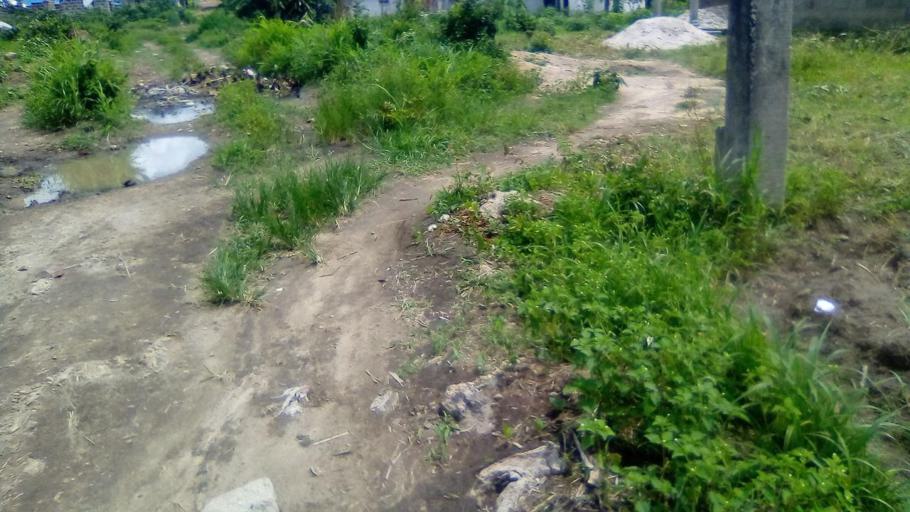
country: SL
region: Southern Province
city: Bo
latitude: 7.9327
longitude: -11.7423
